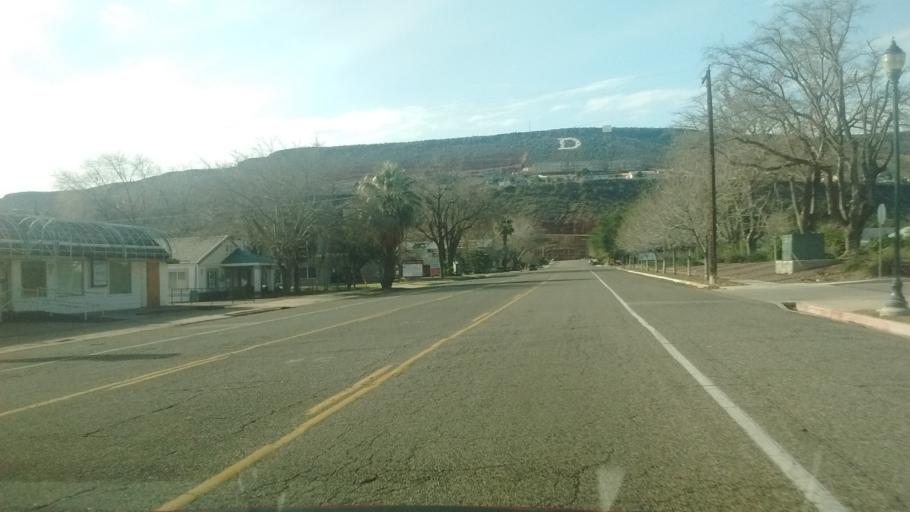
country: US
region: Utah
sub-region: Washington County
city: Saint George
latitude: 37.1083
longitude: -113.5881
